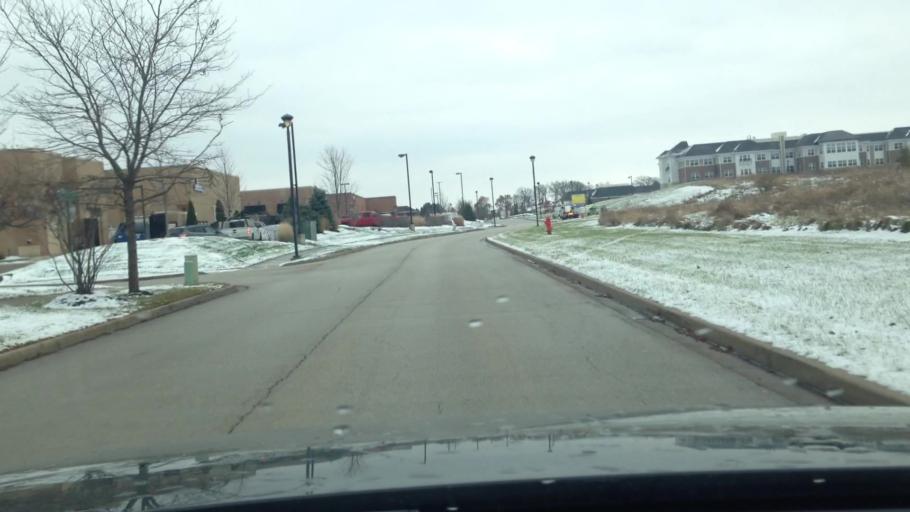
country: US
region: Illinois
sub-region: McHenry County
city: Huntley
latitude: 42.1523
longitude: -88.4344
